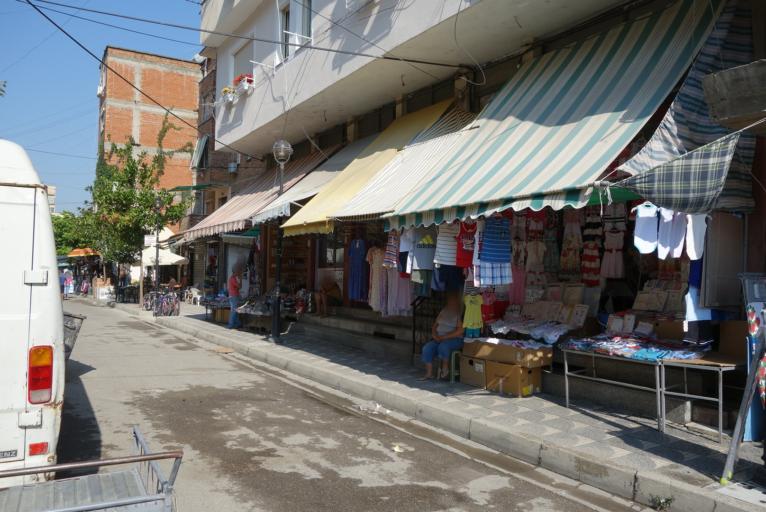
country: AL
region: Tirane
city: Tirana
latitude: 41.3269
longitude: 19.8145
